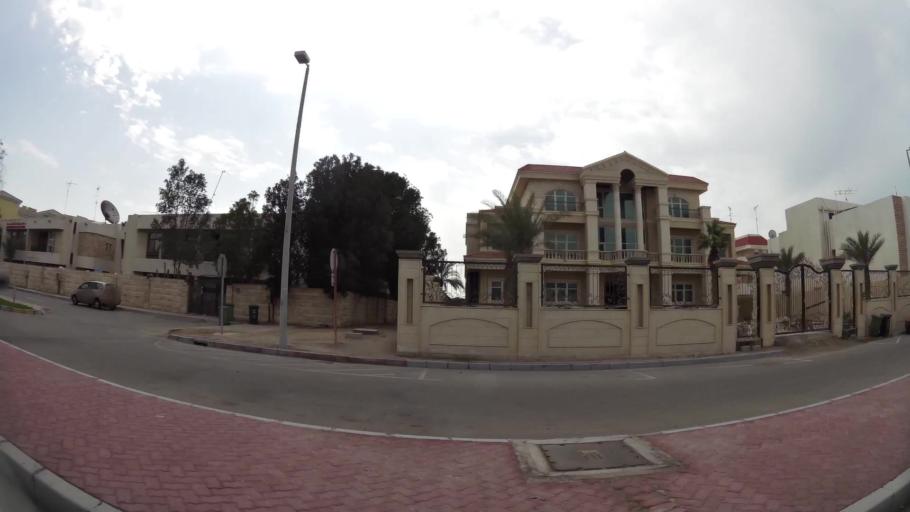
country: AE
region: Abu Dhabi
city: Abu Dhabi
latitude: 24.4598
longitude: 54.3717
